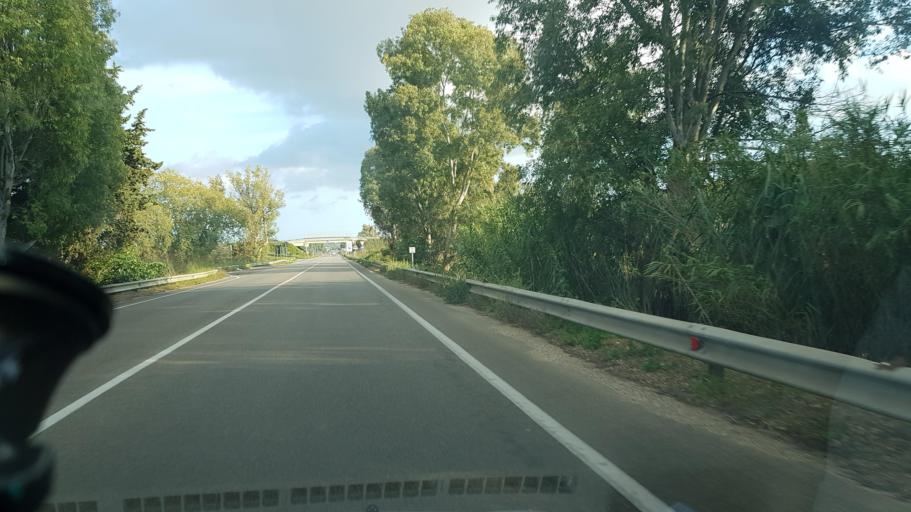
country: IT
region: Apulia
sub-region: Provincia di Lecce
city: Acquarica del Capo
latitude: 39.9028
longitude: 18.2466
